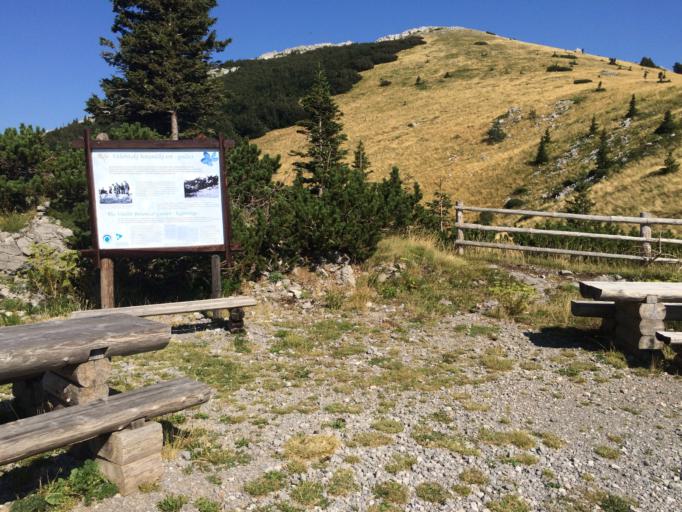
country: HR
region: Licko-Senjska
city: Senj
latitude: 44.8087
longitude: 14.9750
